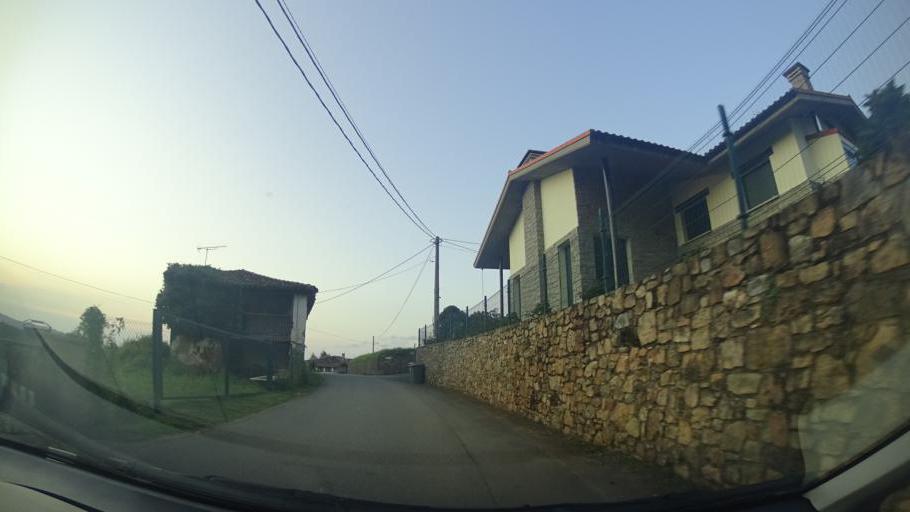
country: ES
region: Asturias
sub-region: Province of Asturias
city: Colunga
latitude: 43.4587
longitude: -5.2037
